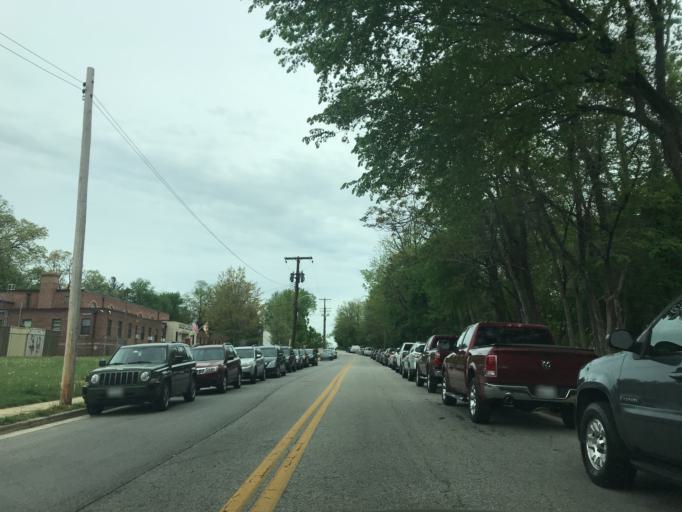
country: US
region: Maryland
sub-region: Baltimore County
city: Catonsville
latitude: 39.2651
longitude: -76.7313
